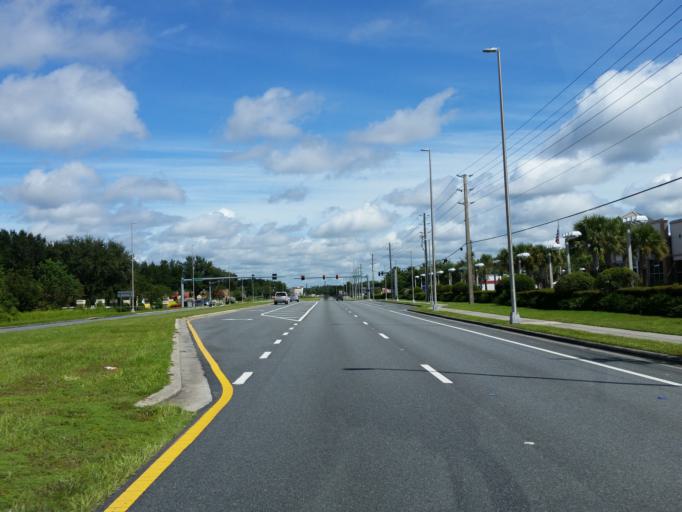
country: US
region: Florida
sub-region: Pasco County
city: Wesley Chapel
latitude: 28.2337
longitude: -82.3704
